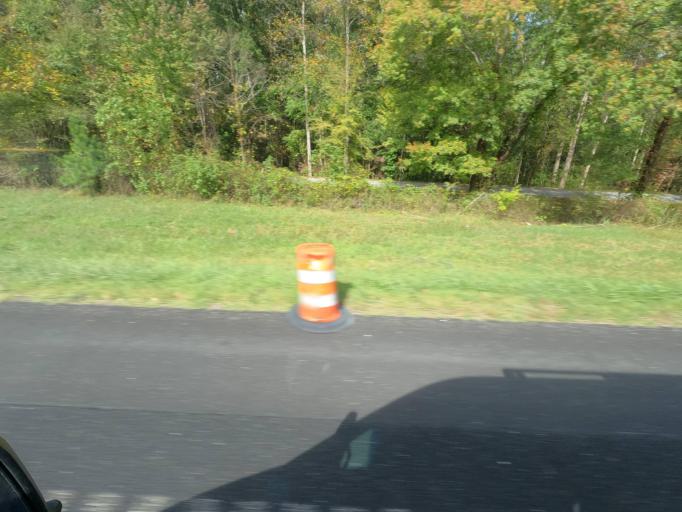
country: US
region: Tennessee
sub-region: Decatur County
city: Parsons
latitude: 35.8293
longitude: -88.1072
